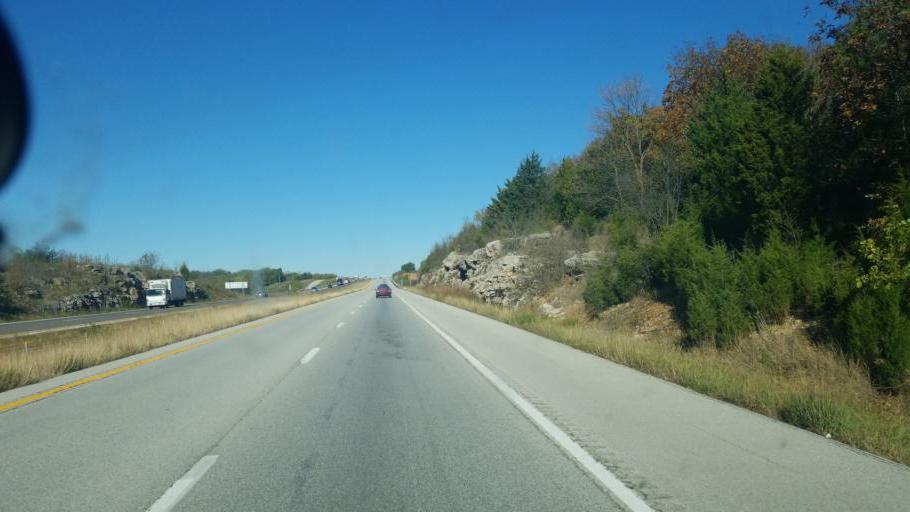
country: US
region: Missouri
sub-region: Cooper County
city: Boonville
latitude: 38.9358
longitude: -92.9794
